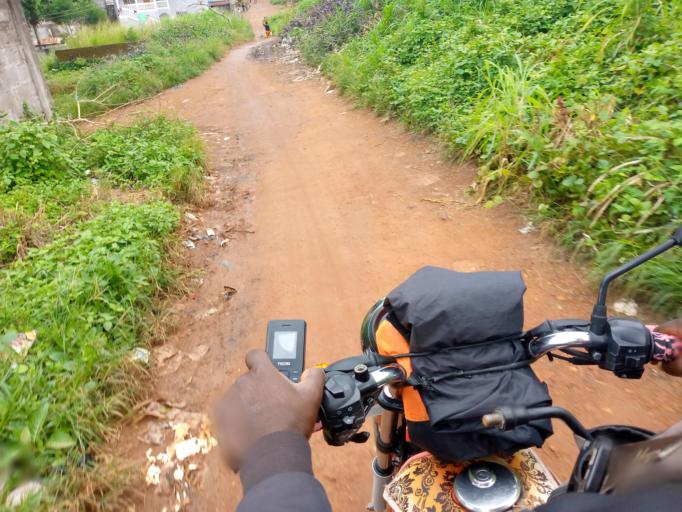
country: SL
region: Eastern Province
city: Kenema
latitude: 7.8732
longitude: -11.1840
